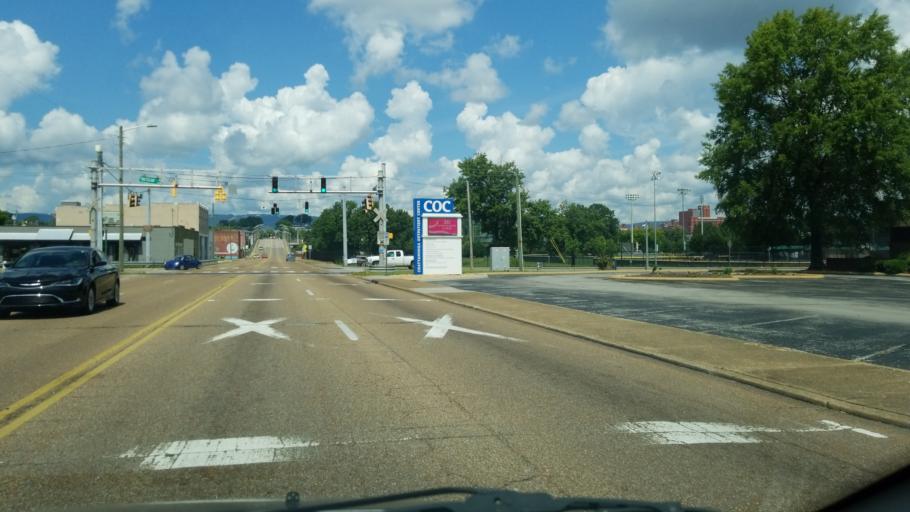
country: US
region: Tennessee
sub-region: Hamilton County
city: Chattanooga
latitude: 35.0387
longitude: -85.2822
